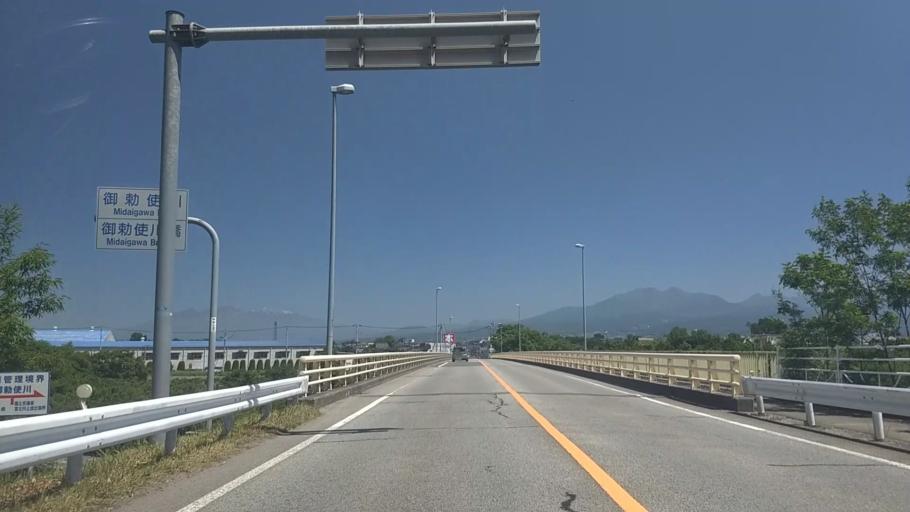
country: JP
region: Yamanashi
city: Nirasaki
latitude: 35.6708
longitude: 138.4648
